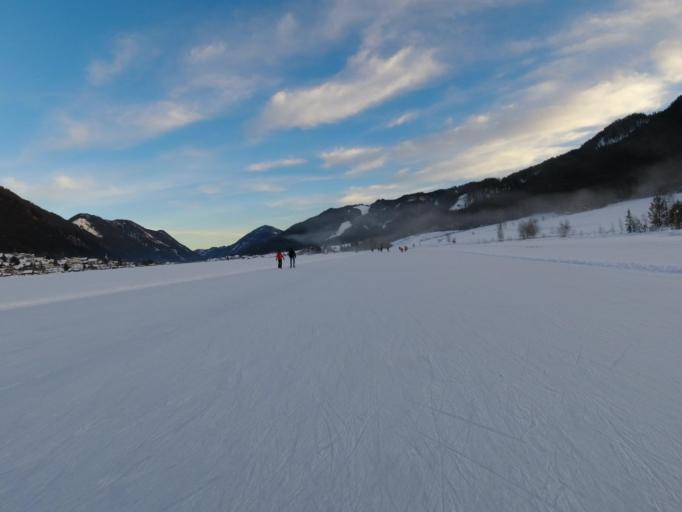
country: AT
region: Carinthia
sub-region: Politischer Bezirk Spittal an der Drau
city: Steinfeld
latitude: 46.7175
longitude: 13.2722
